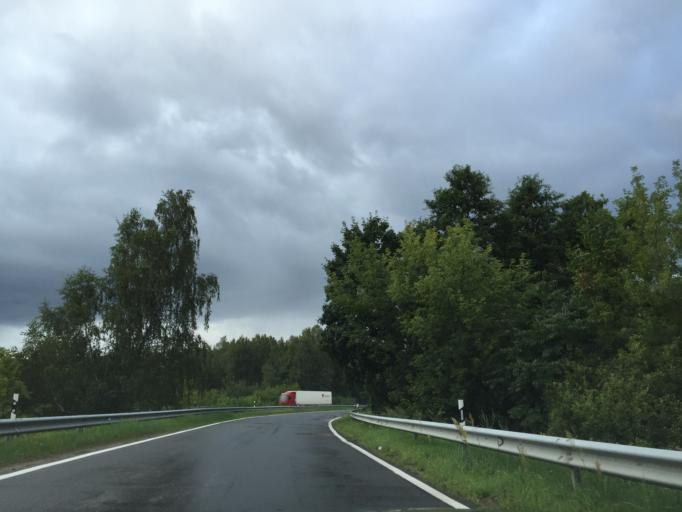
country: LV
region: Babite
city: Pinki
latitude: 56.9561
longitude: 23.9311
